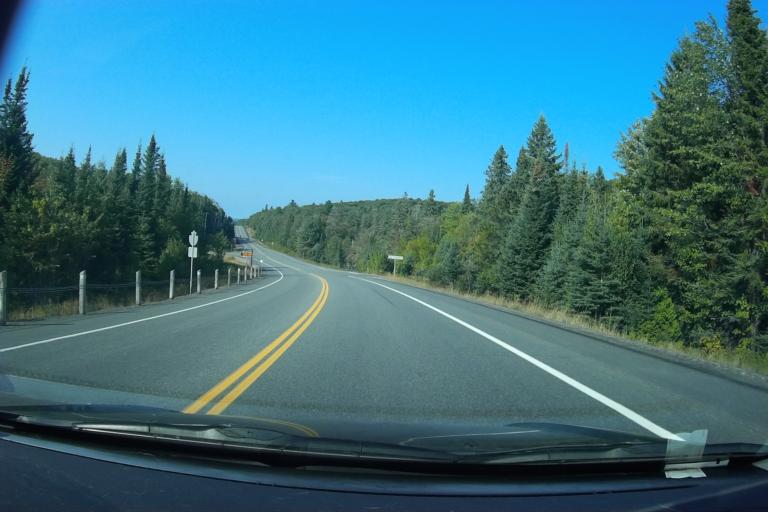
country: CA
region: Ontario
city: Huntsville
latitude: 45.5517
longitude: -78.6365
